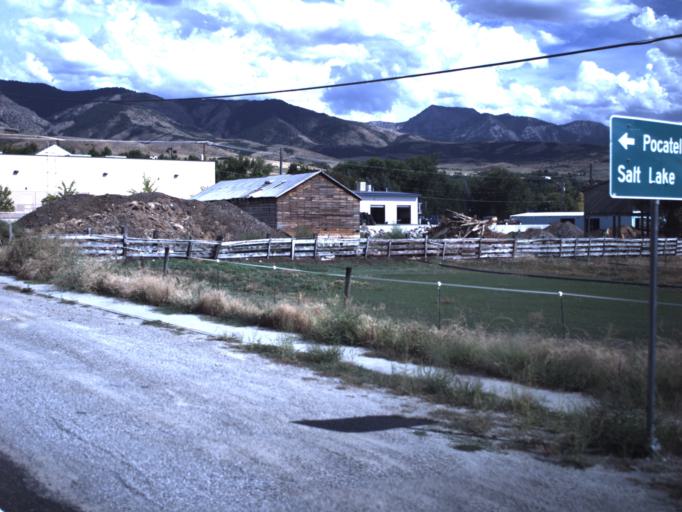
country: US
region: Utah
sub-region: Cache County
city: Richmond
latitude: 41.9227
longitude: -111.8162
